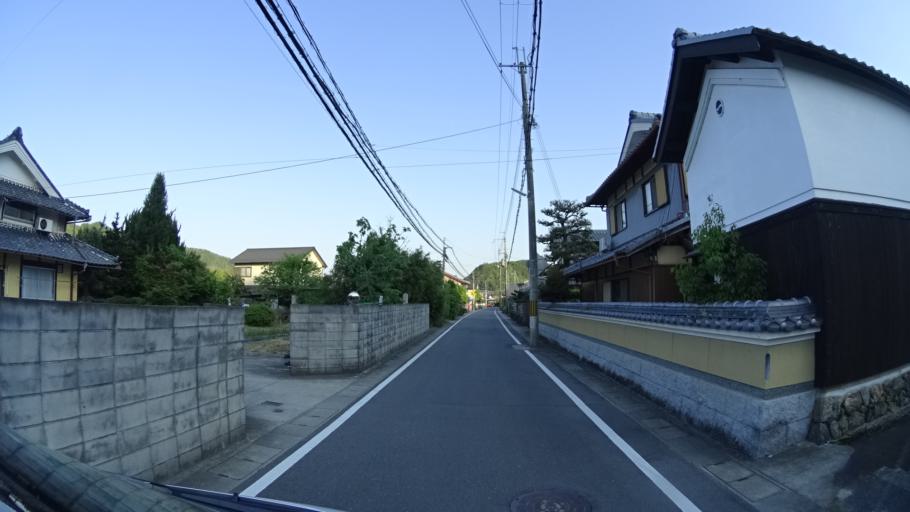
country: JP
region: Kyoto
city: Kameoka
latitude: 35.0916
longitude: 135.5095
